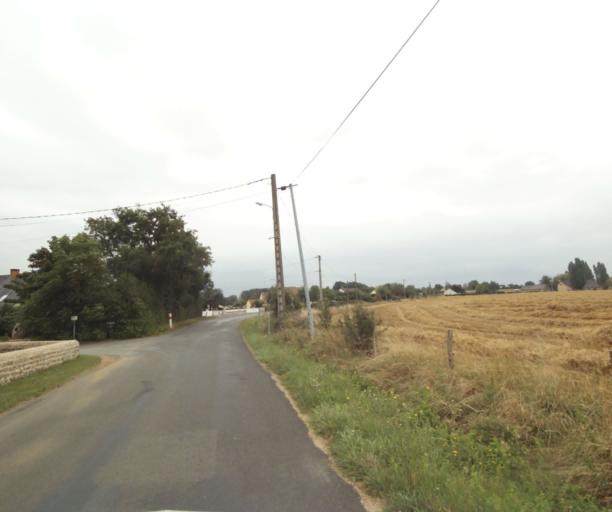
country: FR
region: Pays de la Loire
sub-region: Departement de la Sarthe
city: Solesmes
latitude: 47.8432
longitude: -0.2929
